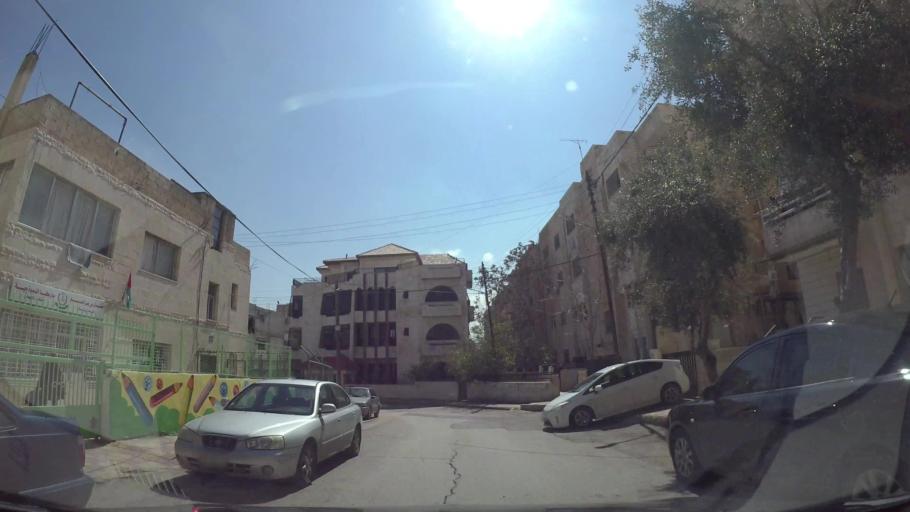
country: JO
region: Amman
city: Amman
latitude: 31.9746
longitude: 35.9885
